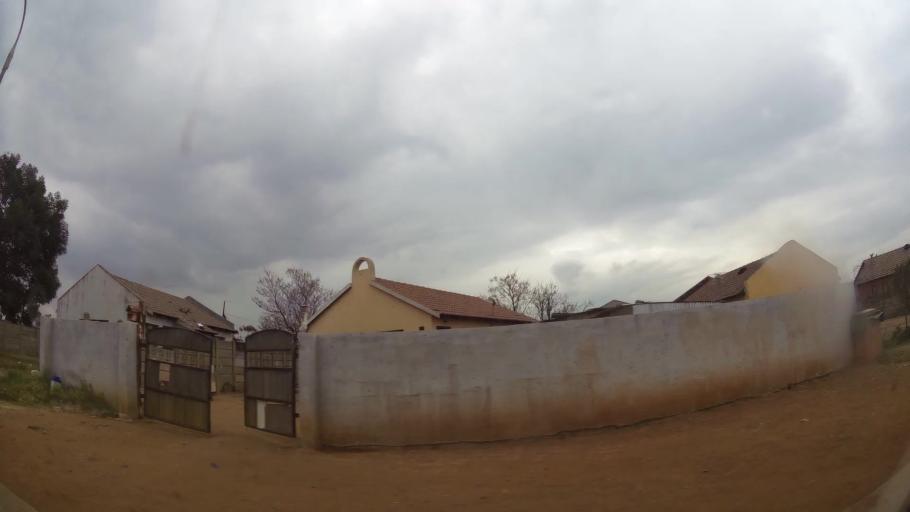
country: ZA
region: Gauteng
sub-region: Ekurhuleni Metropolitan Municipality
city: Germiston
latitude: -26.3821
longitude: 28.1356
